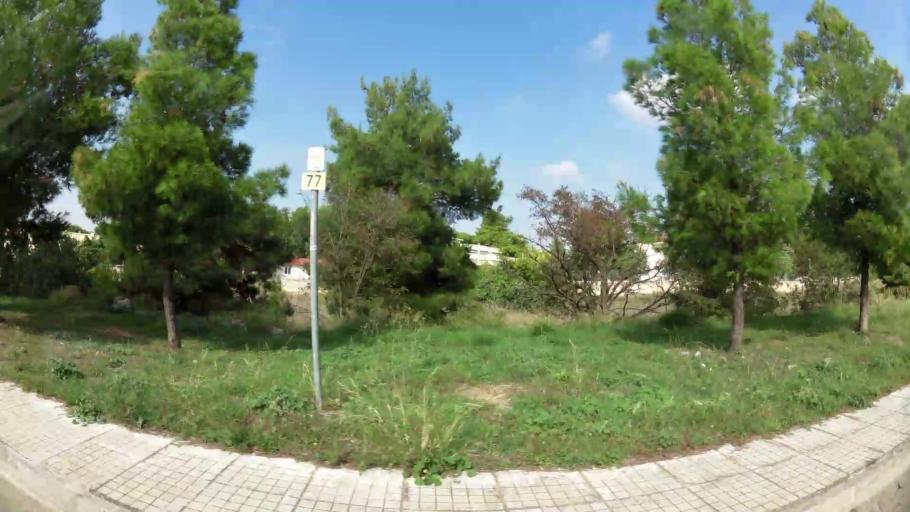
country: GR
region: Attica
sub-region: Nomarchia Athinas
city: Papagou
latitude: 37.9852
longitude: 23.7860
